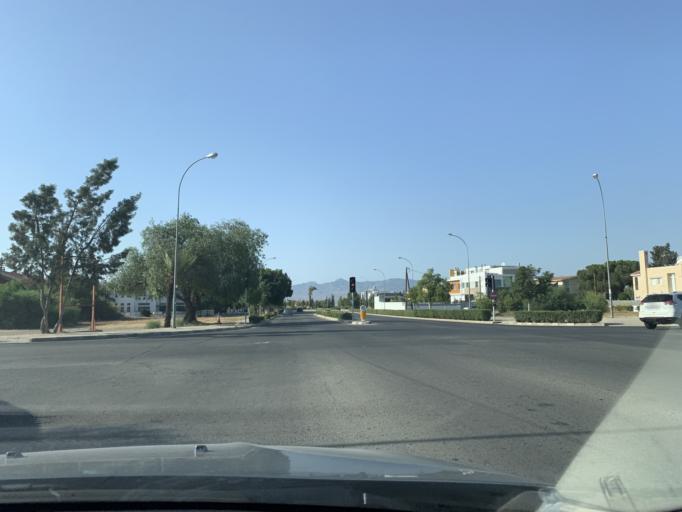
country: CY
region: Lefkosia
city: Nicosia
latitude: 35.1485
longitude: 33.3812
